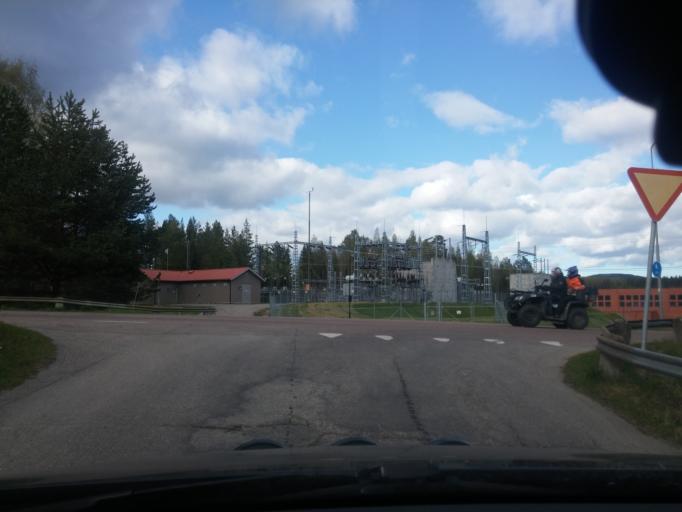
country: SE
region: Gaevleborg
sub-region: Bollnas Kommun
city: Arbra
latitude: 61.4766
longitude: 16.3848
